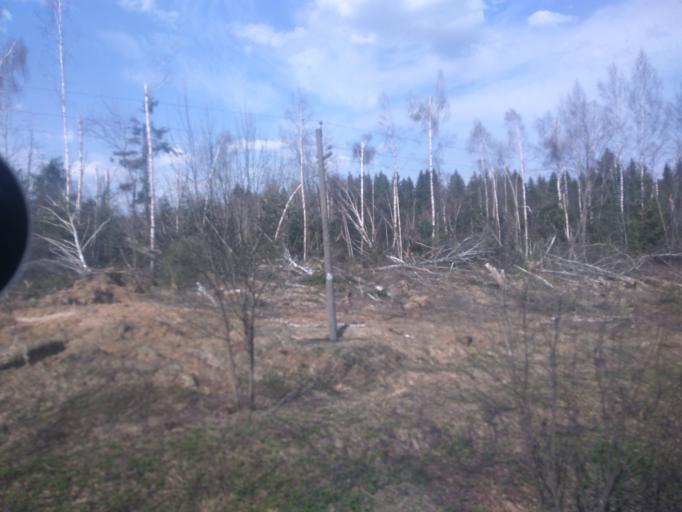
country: RU
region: Moskovskaya
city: Budenovetc
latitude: 56.3220
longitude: 37.7176
